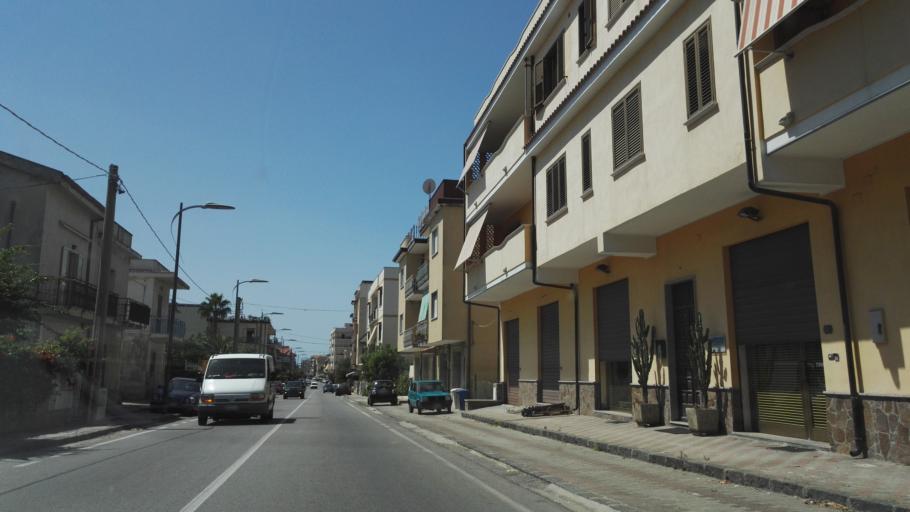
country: IT
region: Calabria
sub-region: Provincia di Reggio Calabria
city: Monasterace Marina
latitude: 38.4426
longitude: 16.5773
